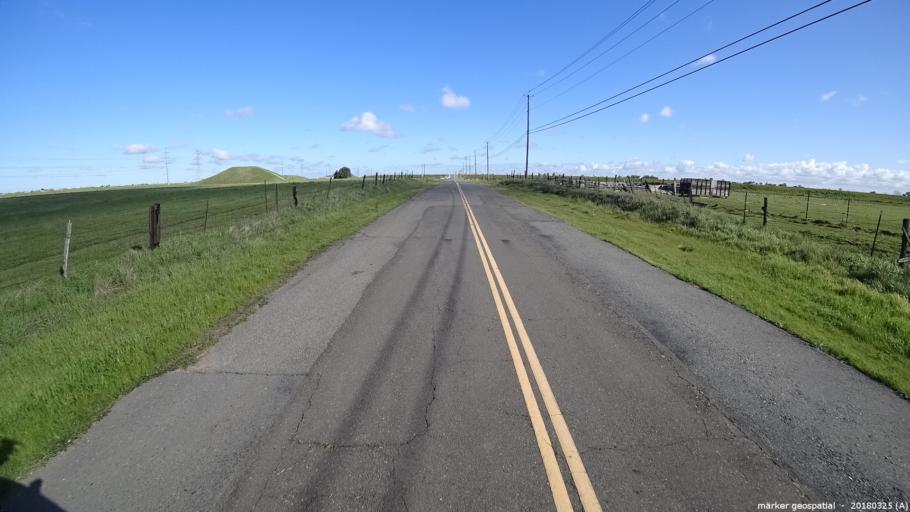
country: US
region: California
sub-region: Sacramento County
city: Rio Linda
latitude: 38.6714
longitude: -121.4841
